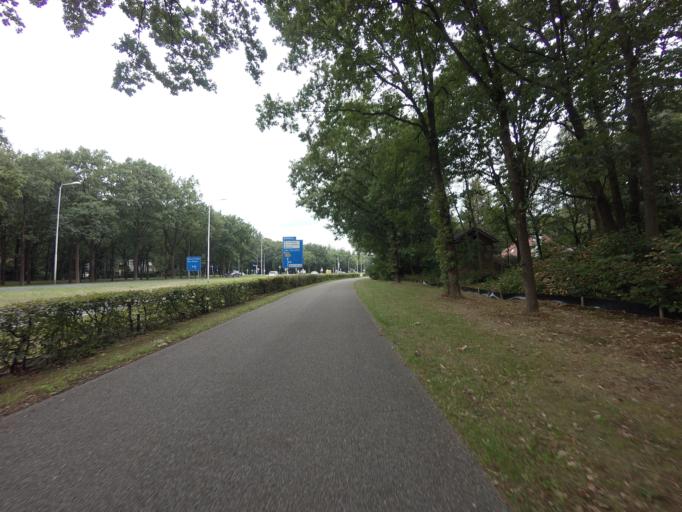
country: NL
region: Utrecht
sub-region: Gemeente Zeist
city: Zeist
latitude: 52.1280
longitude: 5.2504
